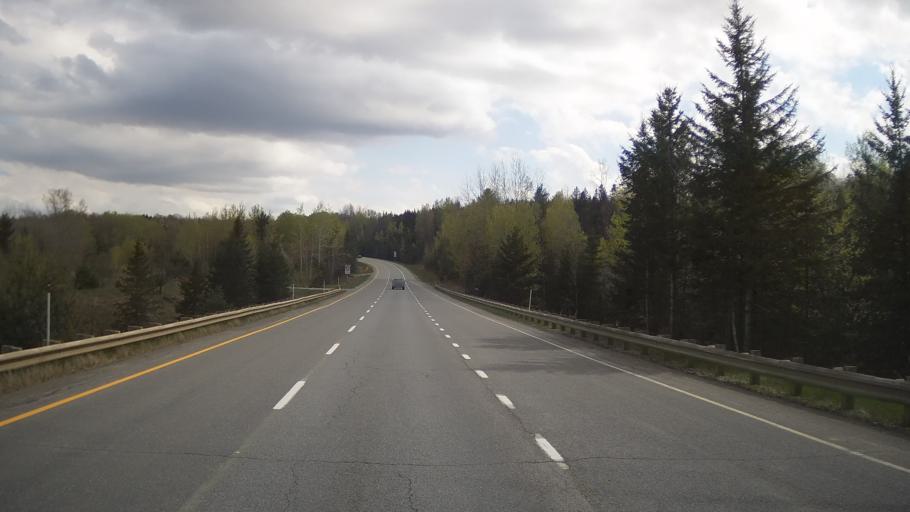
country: CA
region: Quebec
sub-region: Estrie
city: Magog
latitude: 45.1793
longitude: -72.0741
